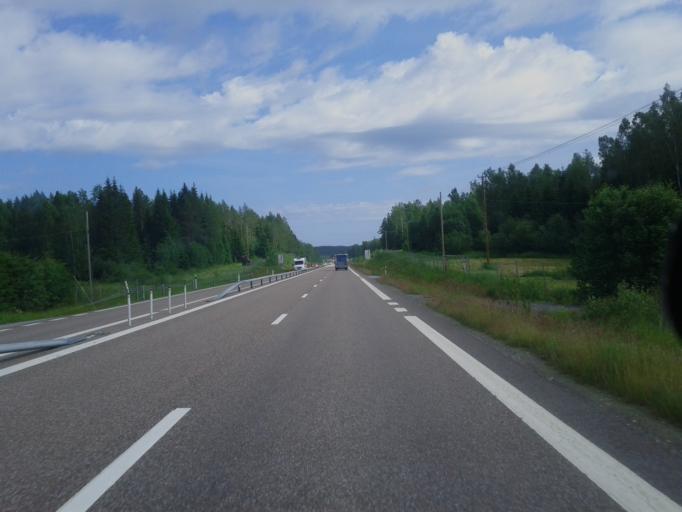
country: SE
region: Vaesternorrland
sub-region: OErnskoeldsviks Kommun
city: Husum
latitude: 63.3202
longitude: 19.0281
